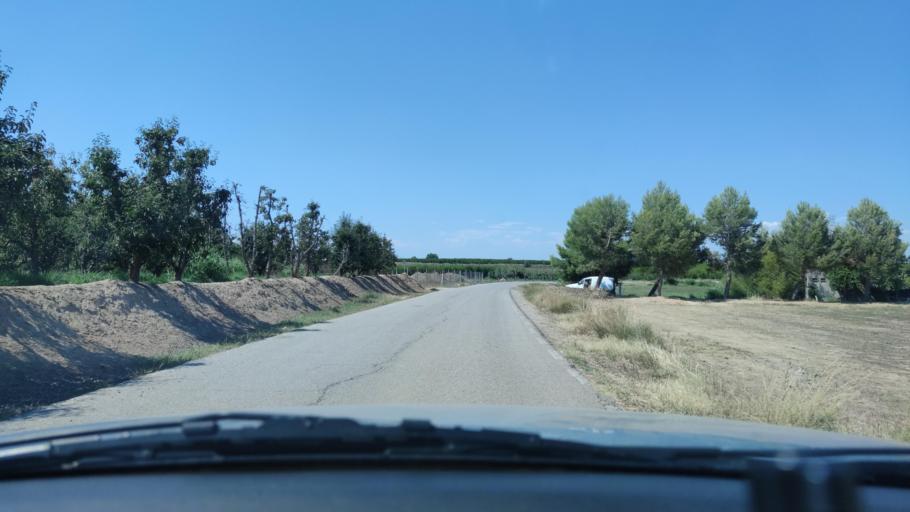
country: ES
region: Catalonia
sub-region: Provincia de Lleida
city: Torrefarrera
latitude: 41.6784
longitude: 0.6163
